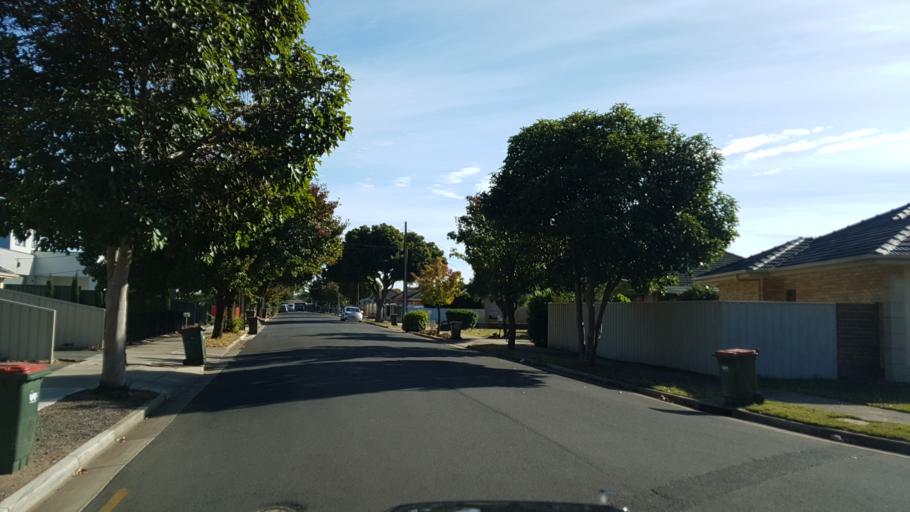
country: AU
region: South Australia
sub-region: City of West Torrens
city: Plympton
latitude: -34.9532
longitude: 138.5480
